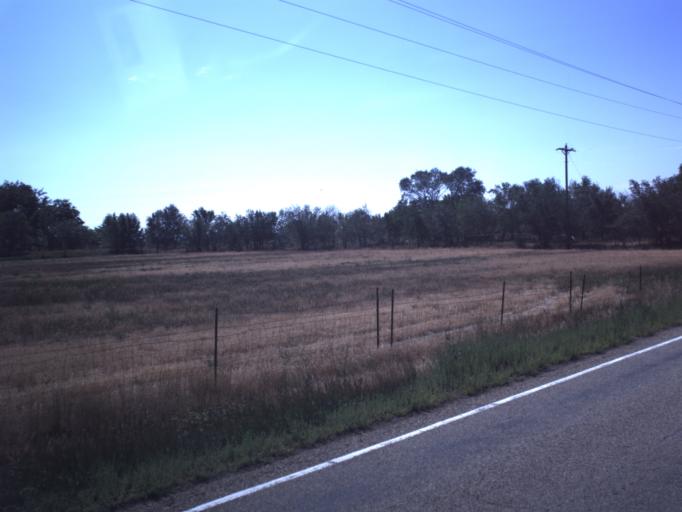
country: US
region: Utah
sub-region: Duchesne County
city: Duchesne
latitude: 40.3531
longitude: -110.2752
